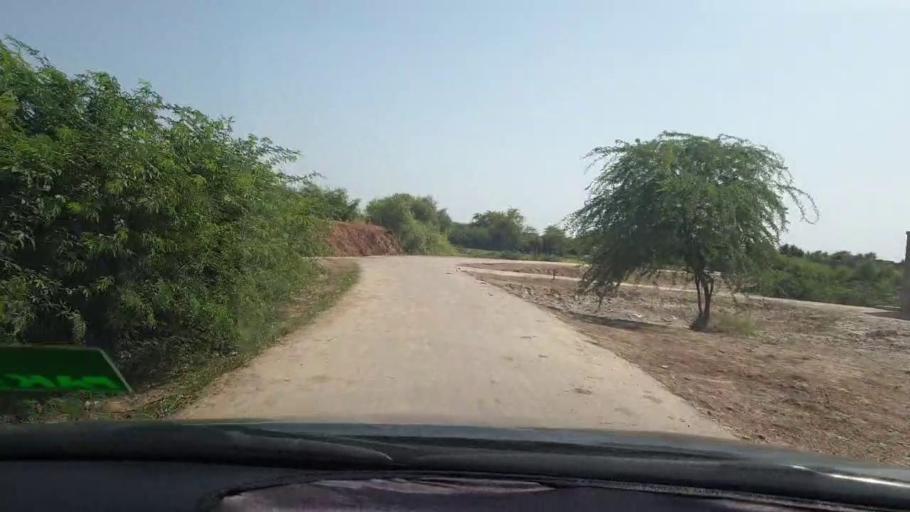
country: PK
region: Sindh
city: Naukot
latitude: 24.9386
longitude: 69.1878
